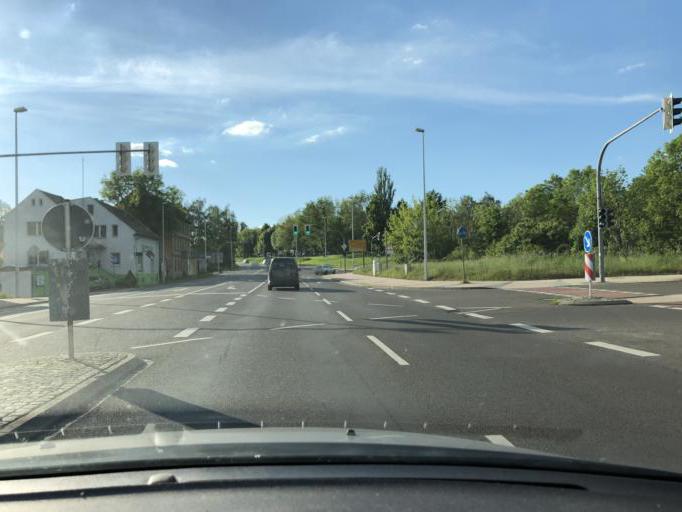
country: DE
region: Thuringia
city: Altenburg
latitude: 50.9932
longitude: 12.4212
